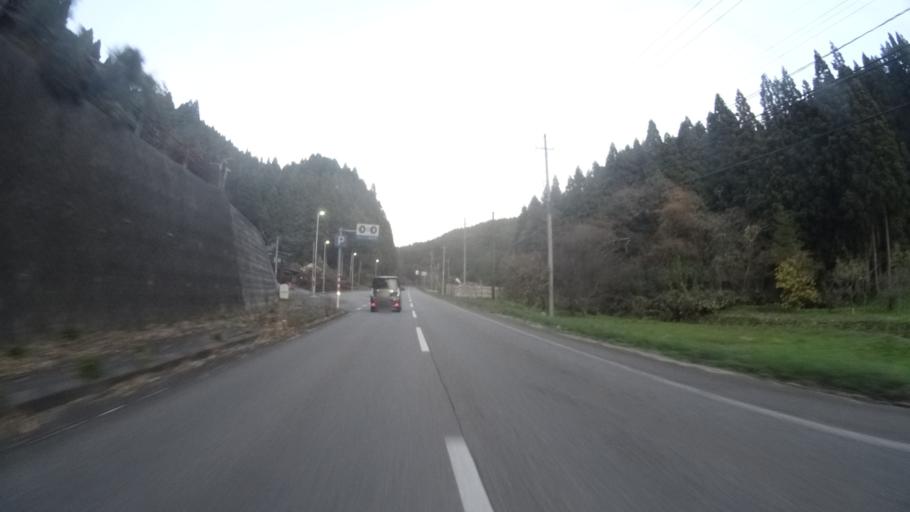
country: JP
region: Ishikawa
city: Nanao
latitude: 37.3142
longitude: 136.8023
